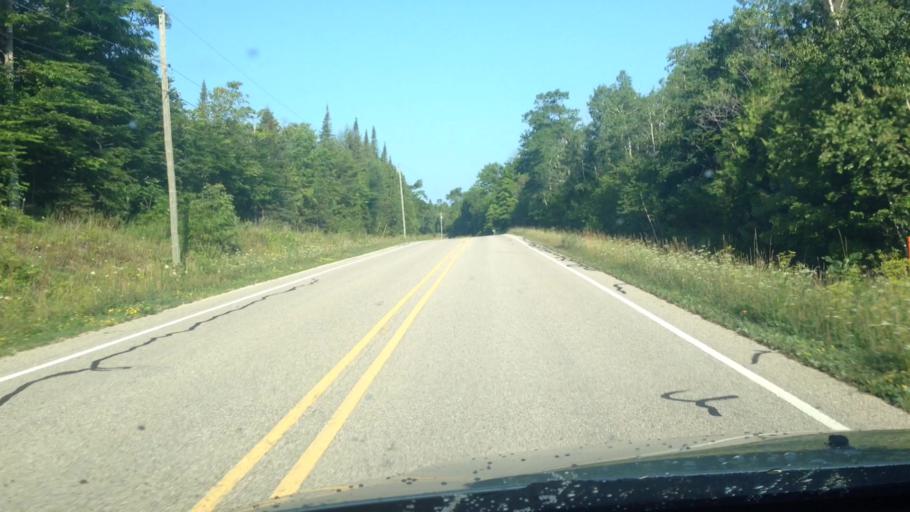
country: US
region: Michigan
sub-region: Mackinac County
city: Saint Ignace
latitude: 45.8936
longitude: -84.8086
